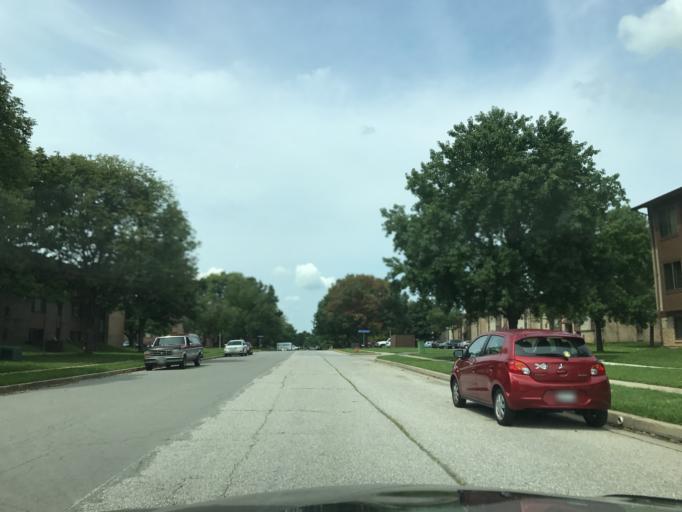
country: US
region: Maryland
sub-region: Baltimore County
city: Essex
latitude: 39.2986
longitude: -76.4432
